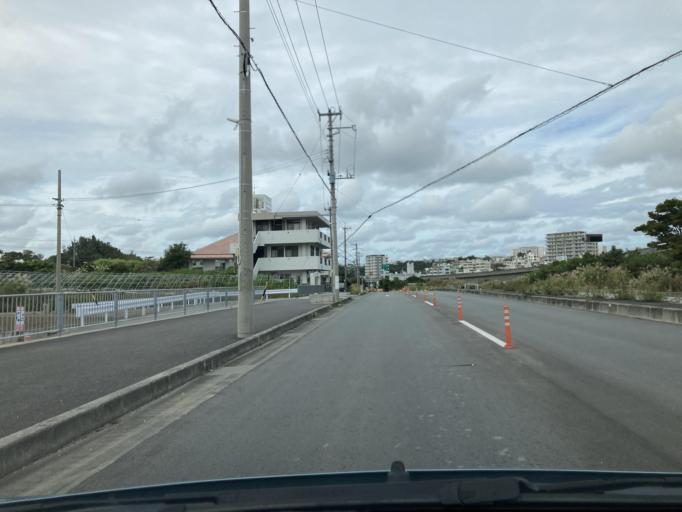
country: JP
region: Okinawa
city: Tomigusuku
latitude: 26.1728
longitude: 127.6754
